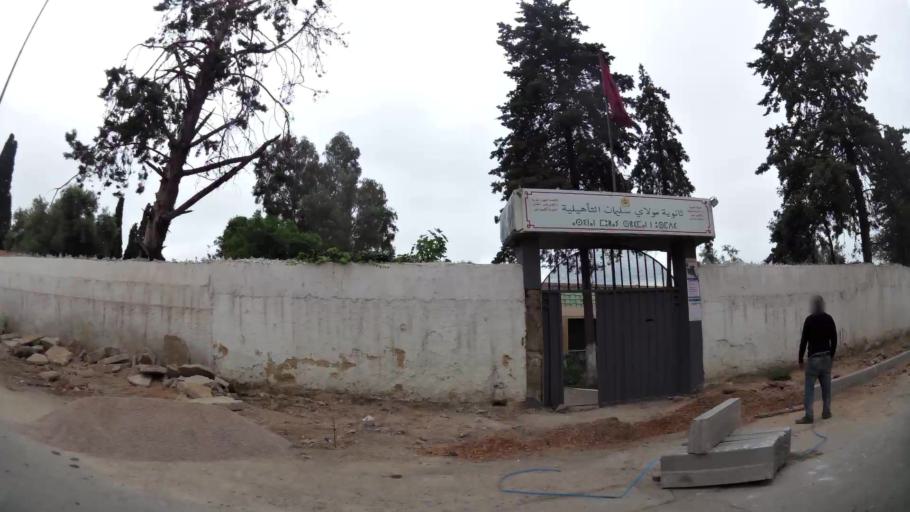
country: MA
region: Fes-Boulemane
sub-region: Fes
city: Fes
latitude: 34.0298
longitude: -5.0002
